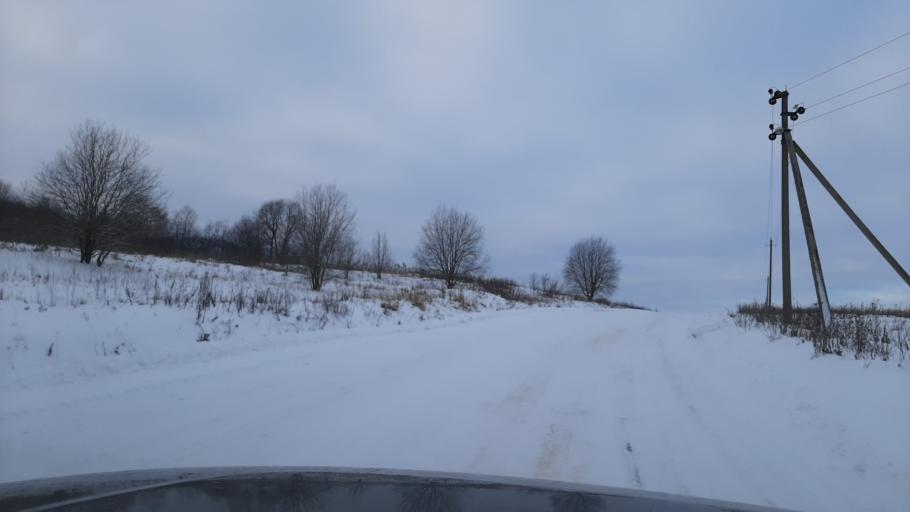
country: RU
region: Kostroma
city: Volgorechensk
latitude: 57.4438
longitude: 40.9377
